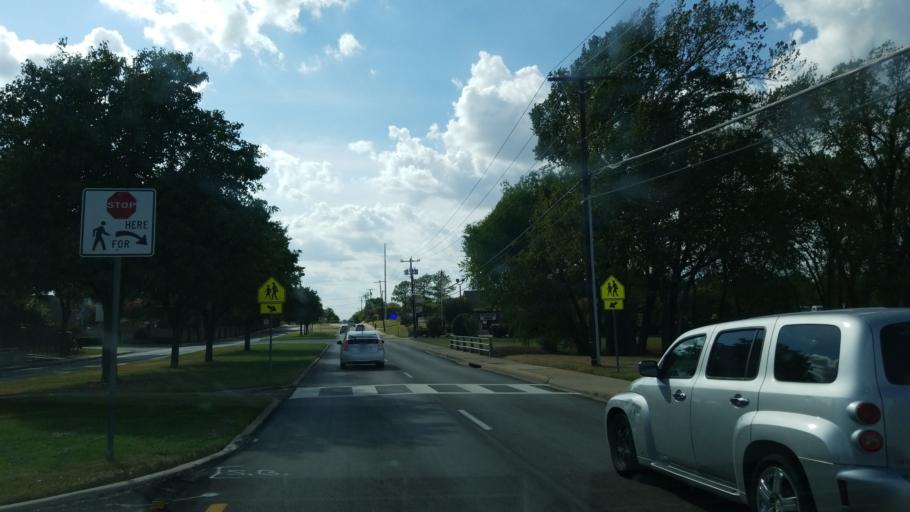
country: US
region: Texas
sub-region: Tarrant County
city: Bedford
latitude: 32.8521
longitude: -97.1188
